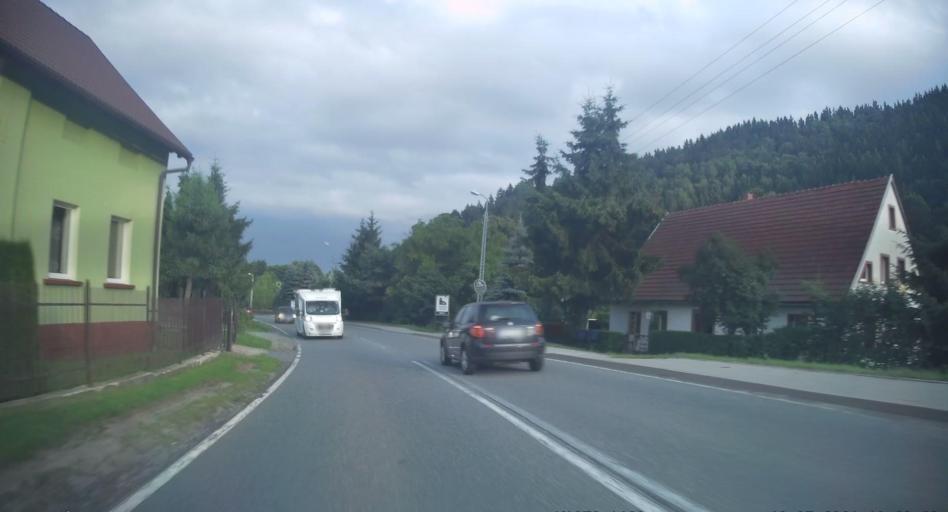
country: PL
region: Lower Silesian Voivodeship
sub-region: Powiat klodzki
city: Ludwikowice Klodzkie
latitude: 50.6223
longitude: 16.4634
